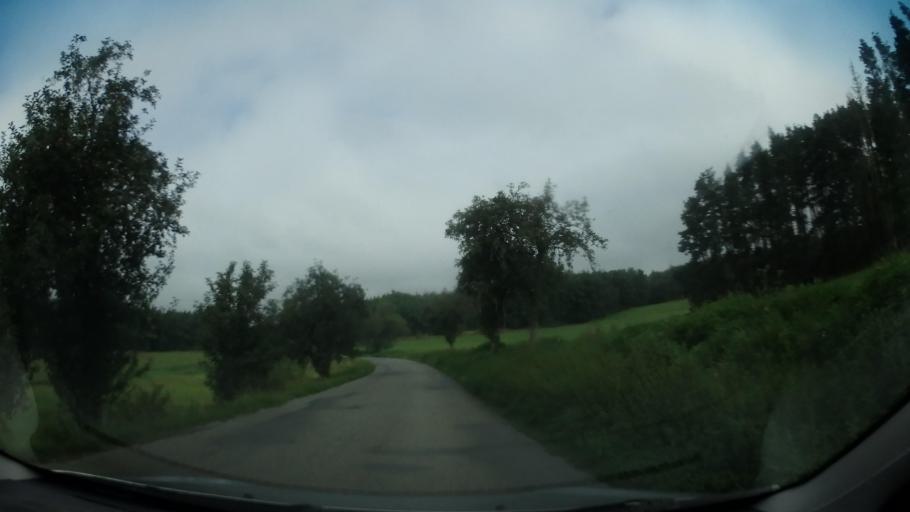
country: CZ
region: Central Bohemia
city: Sedlcany
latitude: 49.7094
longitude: 14.4250
